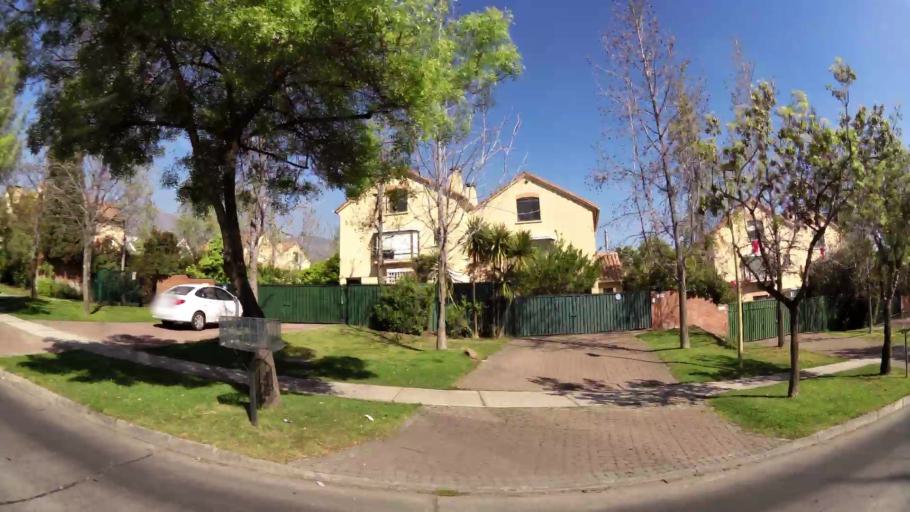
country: CL
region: Santiago Metropolitan
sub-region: Provincia de Santiago
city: Villa Presidente Frei, Nunoa, Santiago, Chile
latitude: -33.4000
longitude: -70.5112
